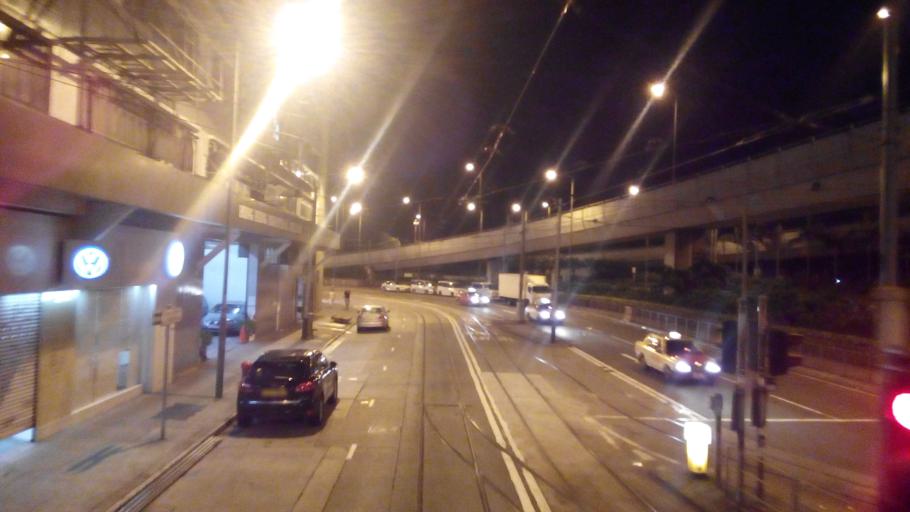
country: HK
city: Hong Kong
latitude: 22.2871
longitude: 114.1337
